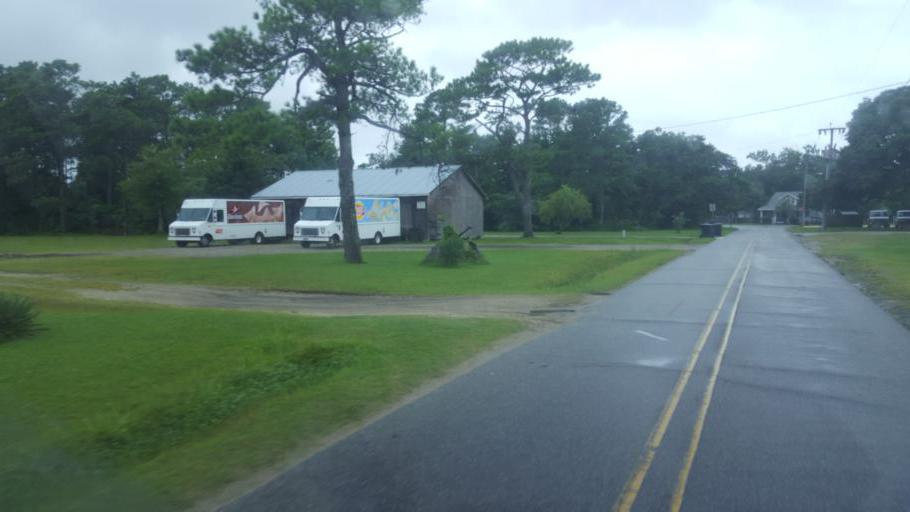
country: US
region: North Carolina
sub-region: Dare County
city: Wanchese
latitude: 35.8421
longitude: -75.6264
